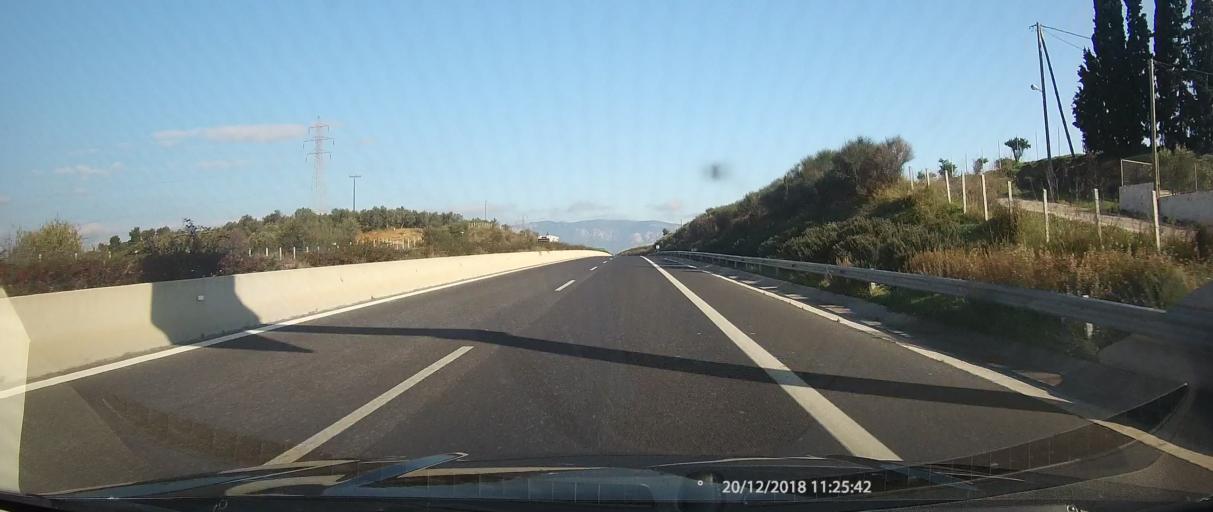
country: GR
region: Peloponnese
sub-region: Nomos Korinthias
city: Arkhaia Korinthos
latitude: 37.9026
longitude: 22.9028
